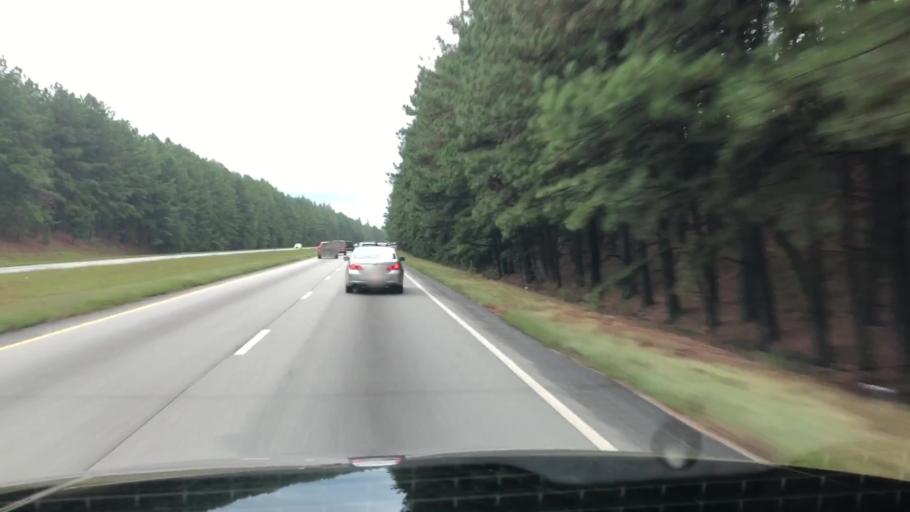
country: US
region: Georgia
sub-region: Cobb County
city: Mableton
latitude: 33.7583
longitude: -84.5924
